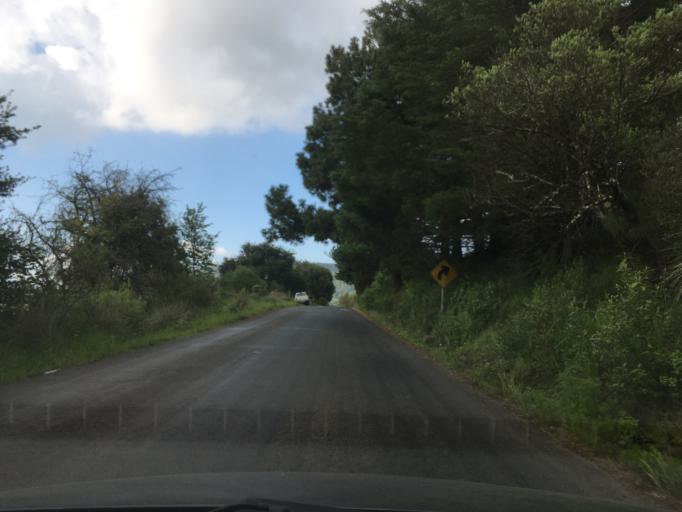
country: MX
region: Michoacan
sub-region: Nahuatzen
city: Sevina
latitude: 19.6182
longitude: -101.9324
